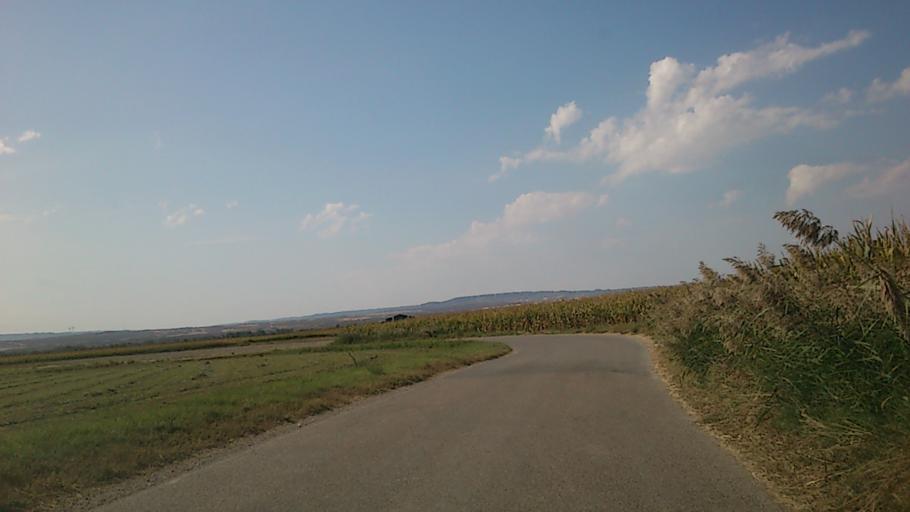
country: ES
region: Aragon
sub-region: Provincia de Zaragoza
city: Puebla de Alfinden
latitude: 41.6210
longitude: -0.7598
